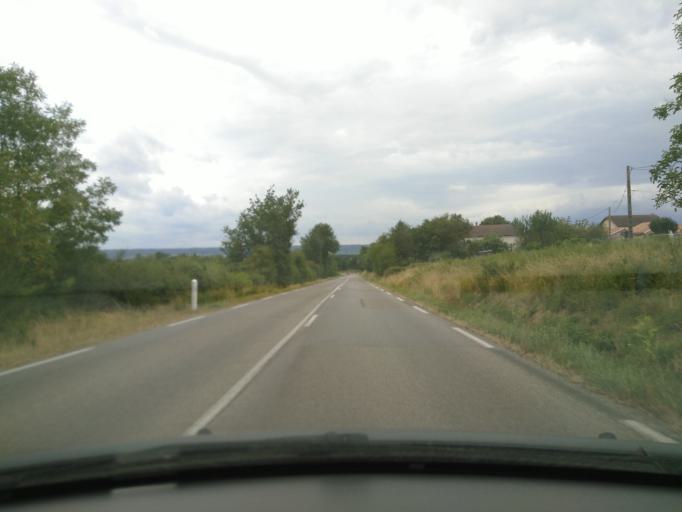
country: FR
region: Rhone-Alpes
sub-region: Departement de l'Isere
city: Beaurepaire
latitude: 45.3625
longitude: 5.0292
